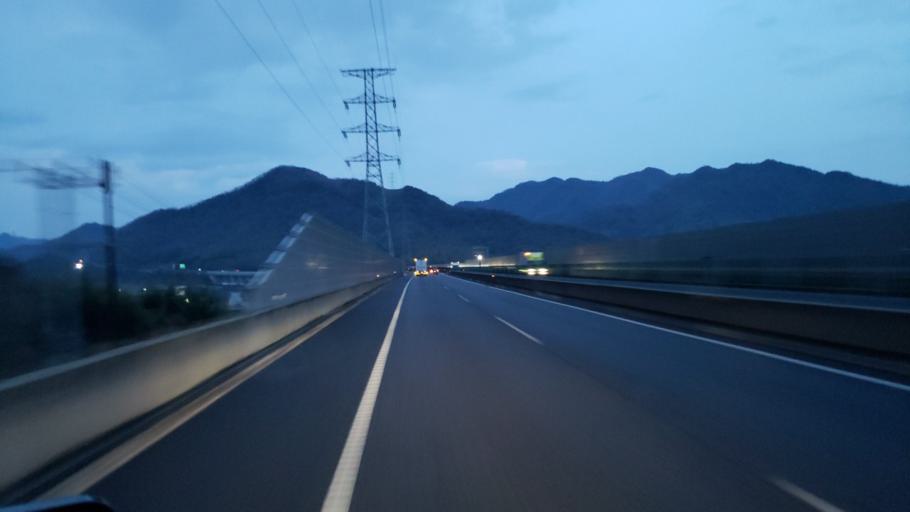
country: JP
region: Hyogo
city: Himeji
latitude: 34.8500
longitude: 134.7494
